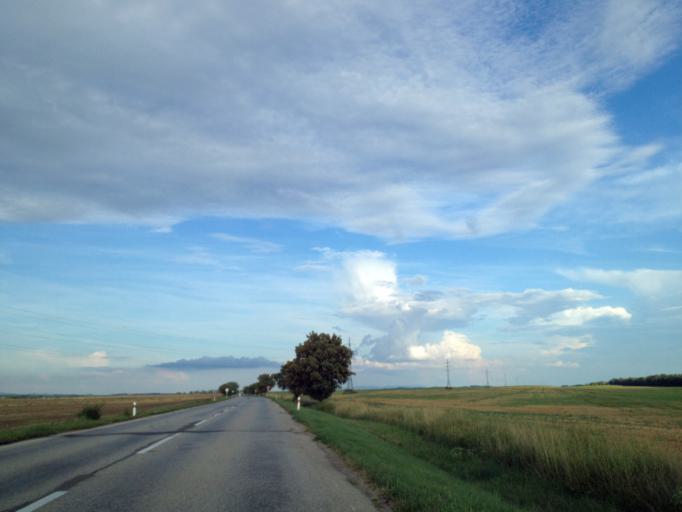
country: SK
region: Nitriansky
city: Svodin
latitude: 47.8983
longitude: 18.3691
